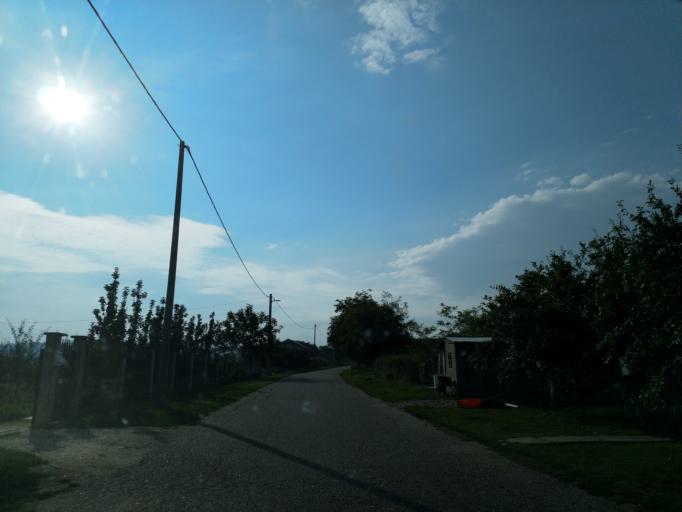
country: RS
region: Central Serbia
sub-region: Pomoravski Okrug
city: Jagodina
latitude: 43.9854
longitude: 21.2166
